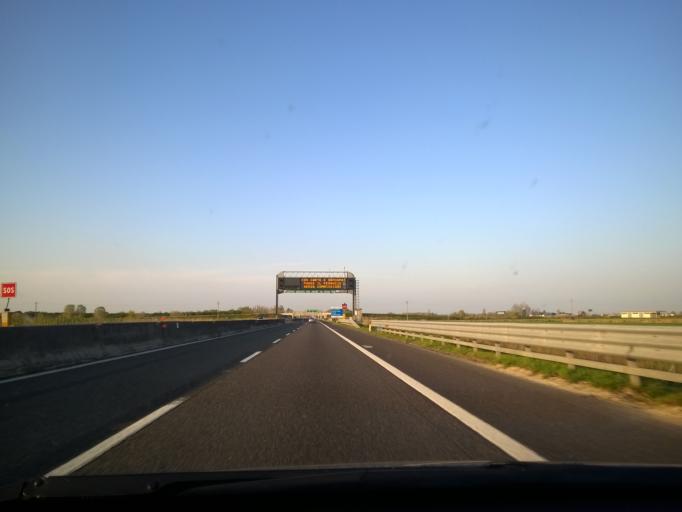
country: IT
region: Emilia-Romagna
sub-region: Provincia di Bologna
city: Altedo
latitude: 44.6824
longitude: 11.4755
